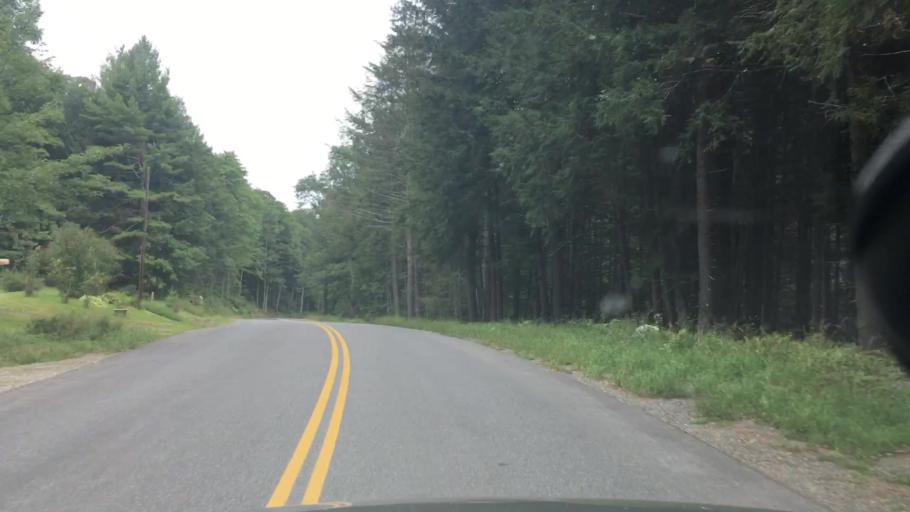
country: US
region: Massachusetts
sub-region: Franklin County
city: Colrain
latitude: 42.7696
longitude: -72.7656
